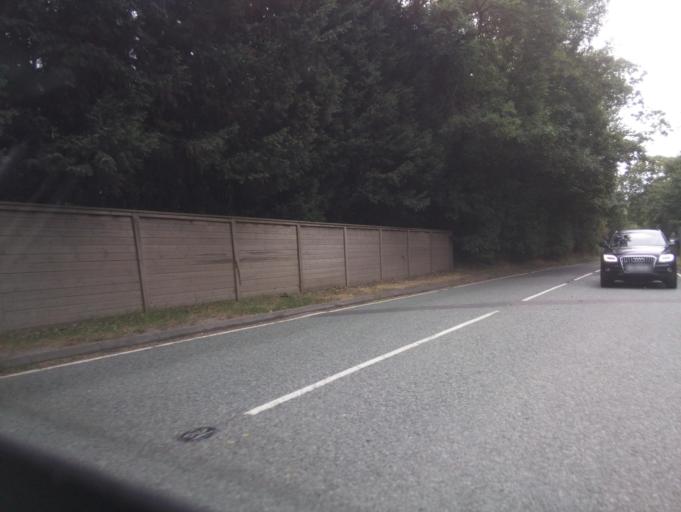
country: GB
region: England
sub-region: Leicestershire
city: Castle Donington
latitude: 52.8219
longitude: -1.3710
